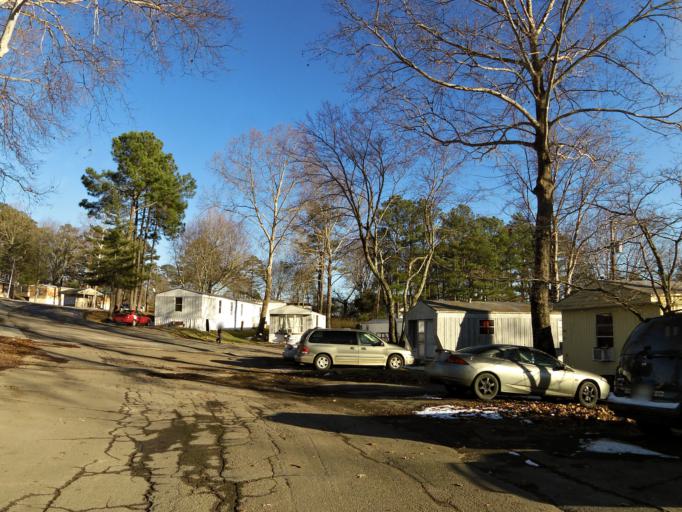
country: US
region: Tennessee
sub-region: Knox County
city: Farragut
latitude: 35.9630
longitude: -84.0608
